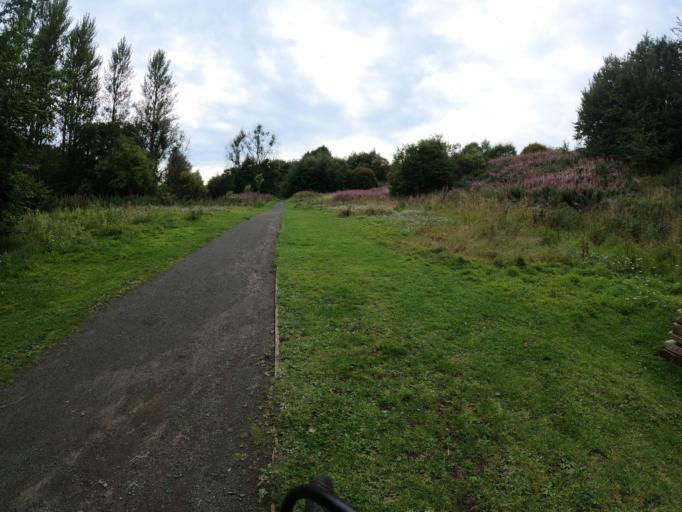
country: GB
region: Scotland
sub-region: West Lothian
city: Livingston
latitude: 55.8626
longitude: -3.5100
